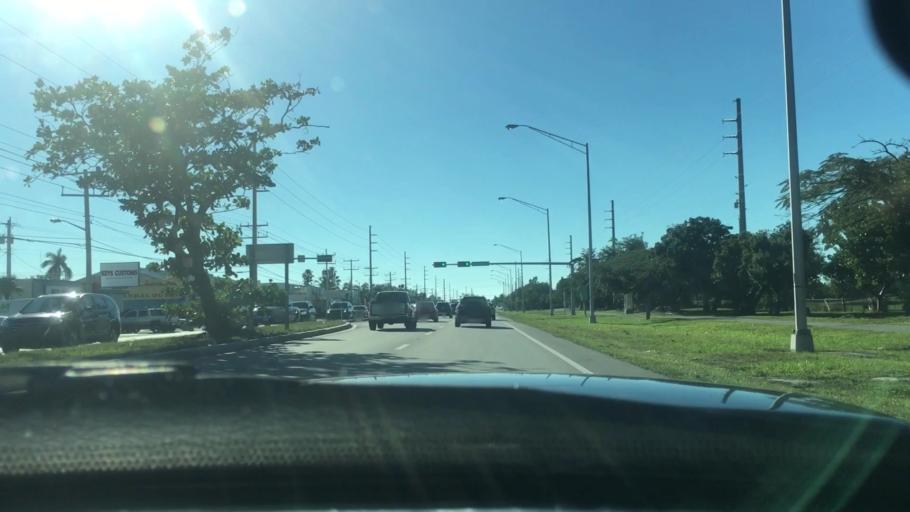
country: US
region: Florida
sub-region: Monroe County
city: Stock Island
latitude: 24.5727
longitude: -81.7440
